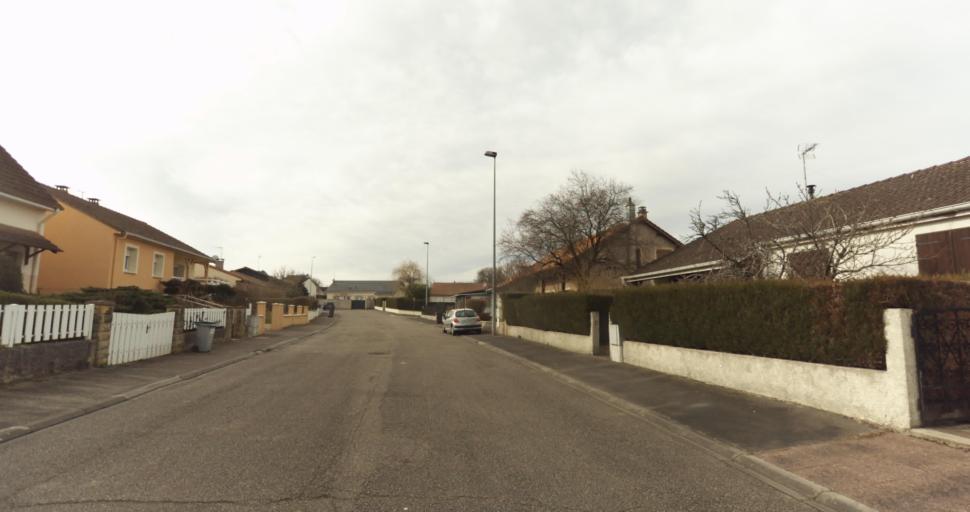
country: FR
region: Lorraine
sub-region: Departement de Meurthe-et-Moselle
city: Jarny
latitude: 49.1589
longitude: 5.8684
